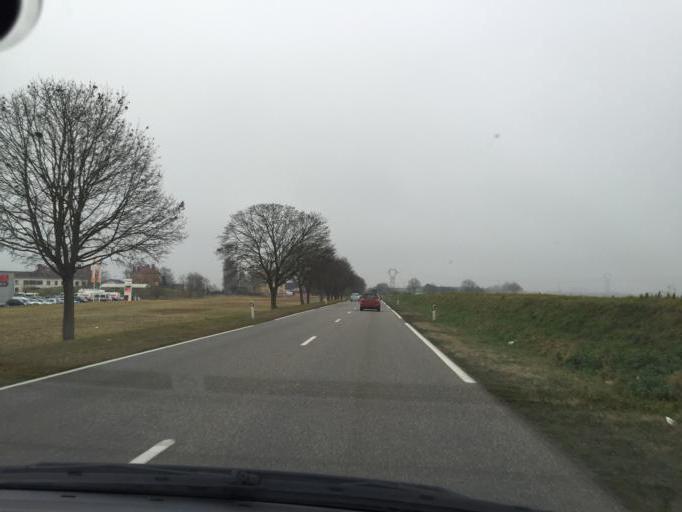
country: FR
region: Alsace
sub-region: Departement du Haut-Rhin
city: Neuf-Brisach
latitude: 48.0093
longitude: 7.5397
